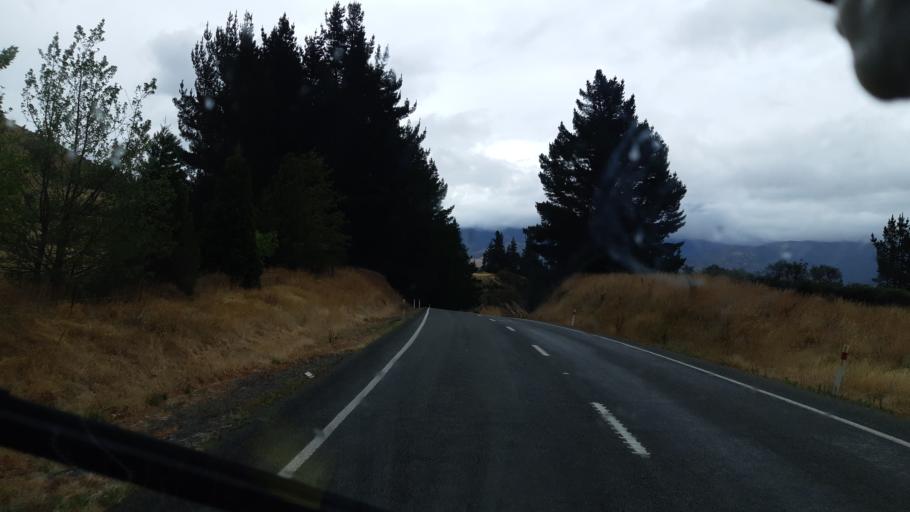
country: NZ
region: Canterbury
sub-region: Hurunui District
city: Amberley
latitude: -42.5827
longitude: 172.7760
